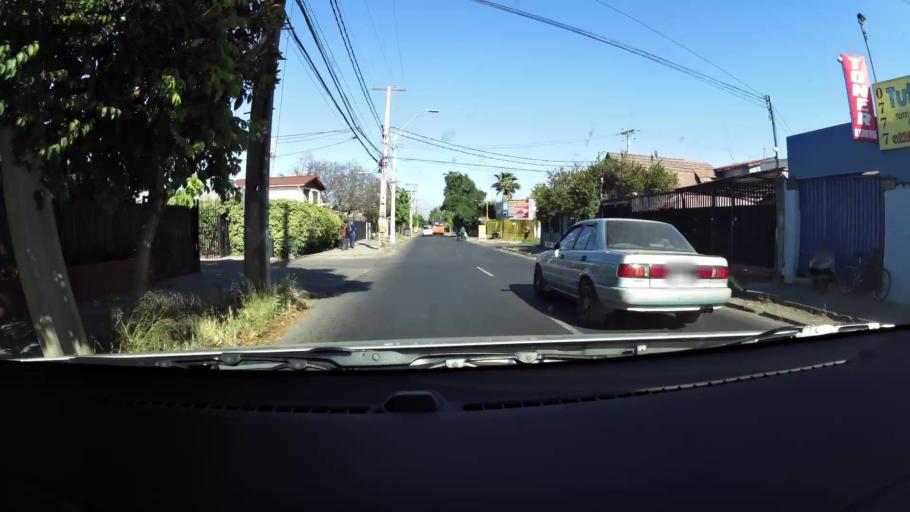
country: CL
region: Santiago Metropolitan
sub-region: Provincia de Maipo
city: San Bernardo
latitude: -33.5403
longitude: -70.6776
